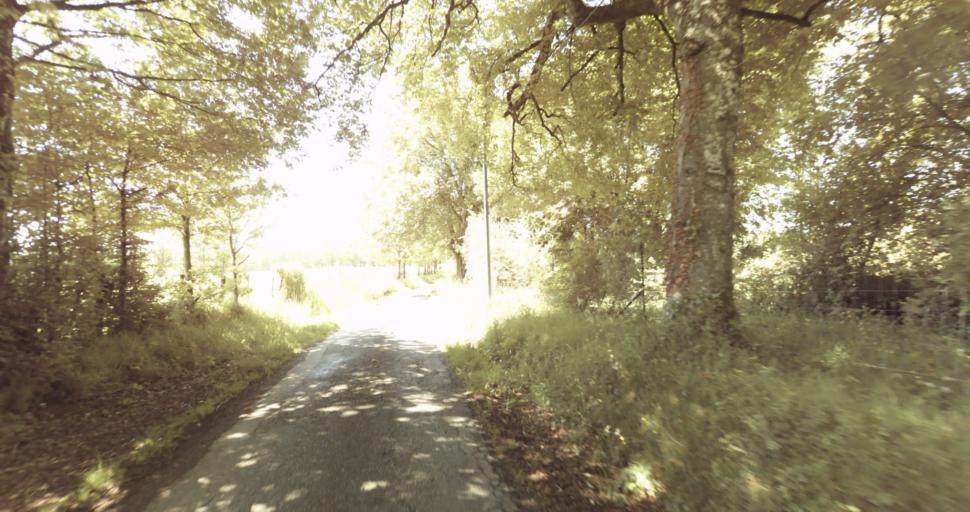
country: FR
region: Limousin
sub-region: Departement de la Haute-Vienne
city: Le Vigen
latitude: 45.7576
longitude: 1.3050
